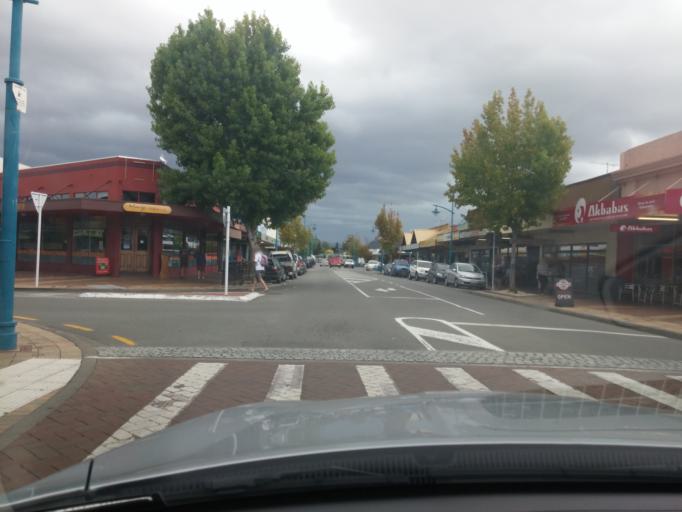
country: NZ
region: Marlborough
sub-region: Marlborough District
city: Blenheim
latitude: -41.5140
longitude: 173.9568
